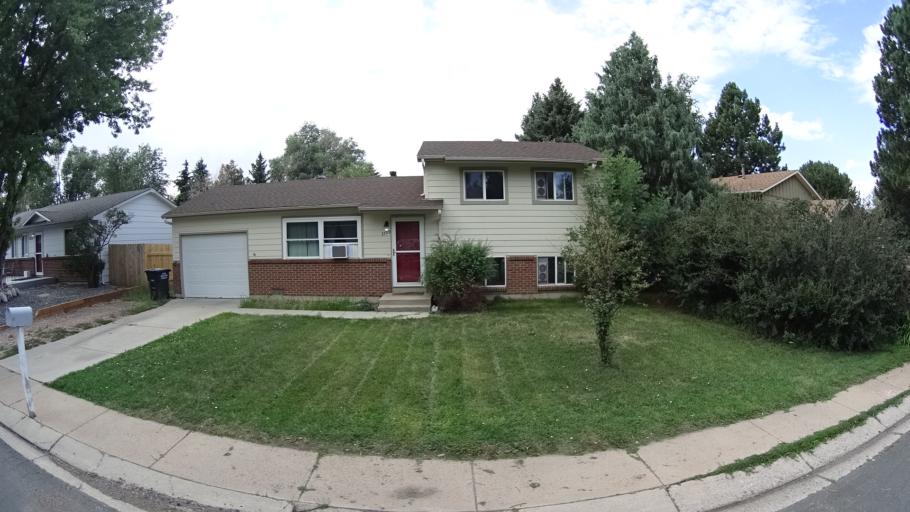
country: US
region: Colorado
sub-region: El Paso County
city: Cimarron Hills
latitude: 38.8991
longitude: -104.7580
